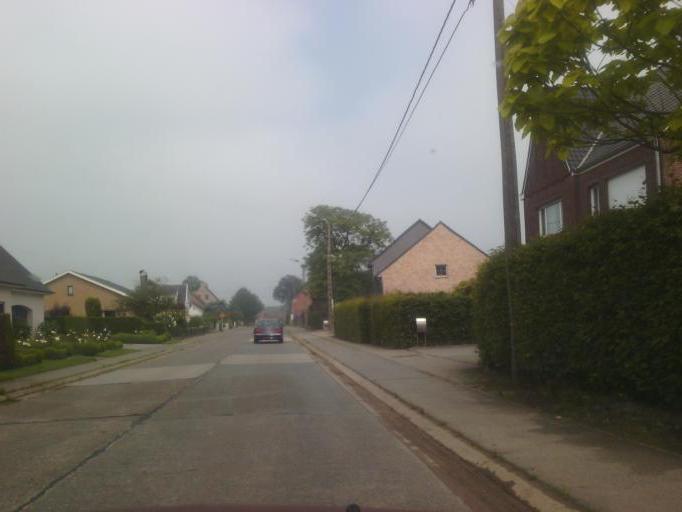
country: BE
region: Flanders
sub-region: Provincie Oost-Vlaanderen
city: Berlare
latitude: 50.9924
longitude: 4.0309
